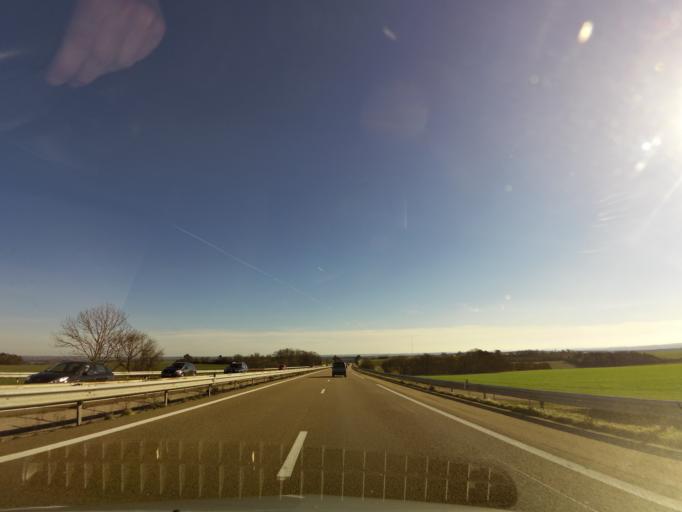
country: FR
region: Bourgogne
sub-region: Departement de l'Yonne
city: Vermenton
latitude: 47.7321
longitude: 3.7412
